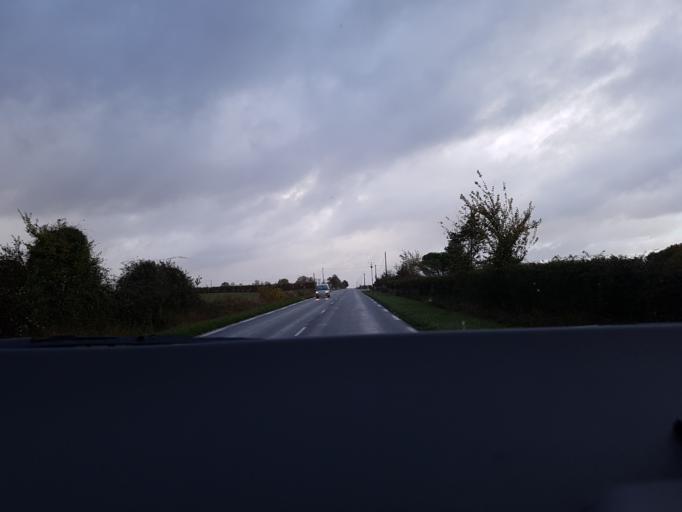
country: FR
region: Poitou-Charentes
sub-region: Departement des Deux-Sevres
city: Melle
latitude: 46.1855
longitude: -0.1820
